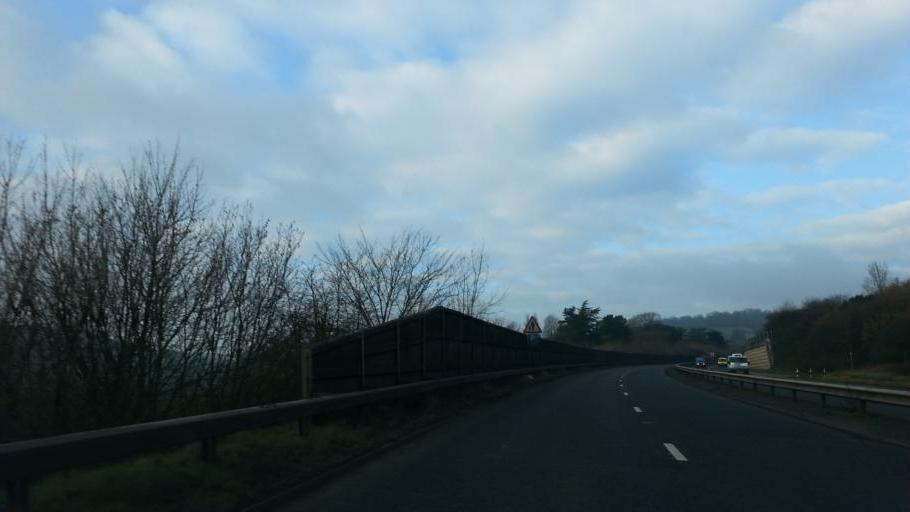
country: GB
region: England
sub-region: Bath and North East Somerset
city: Bath
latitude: 51.4074
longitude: -2.3421
